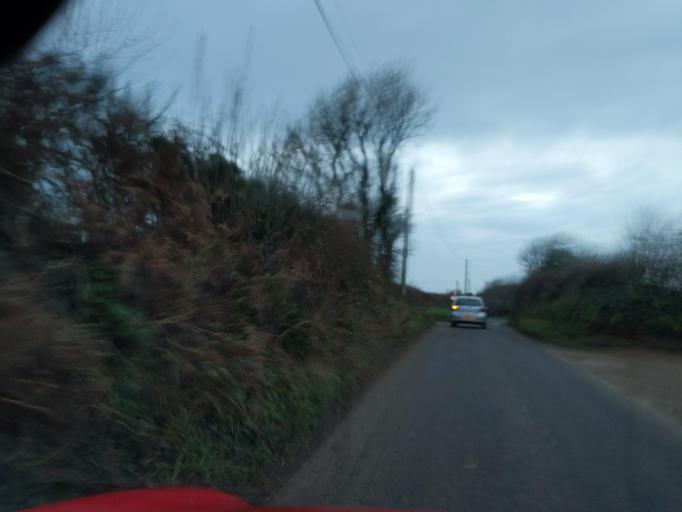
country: GB
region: England
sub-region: Devon
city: Wembury
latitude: 50.3444
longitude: -4.0742
